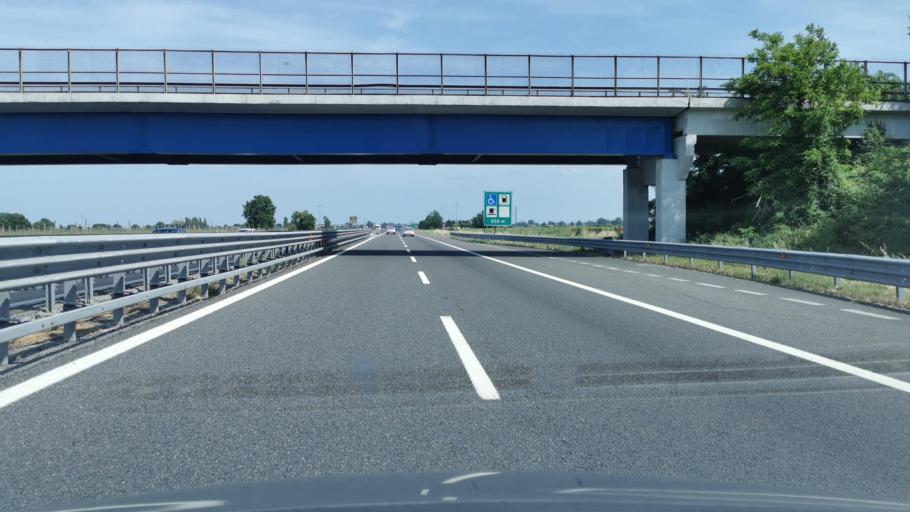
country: IT
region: Emilia-Romagna
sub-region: Provincia di Ravenna
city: Russi
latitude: 44.4044
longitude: 12.0351
